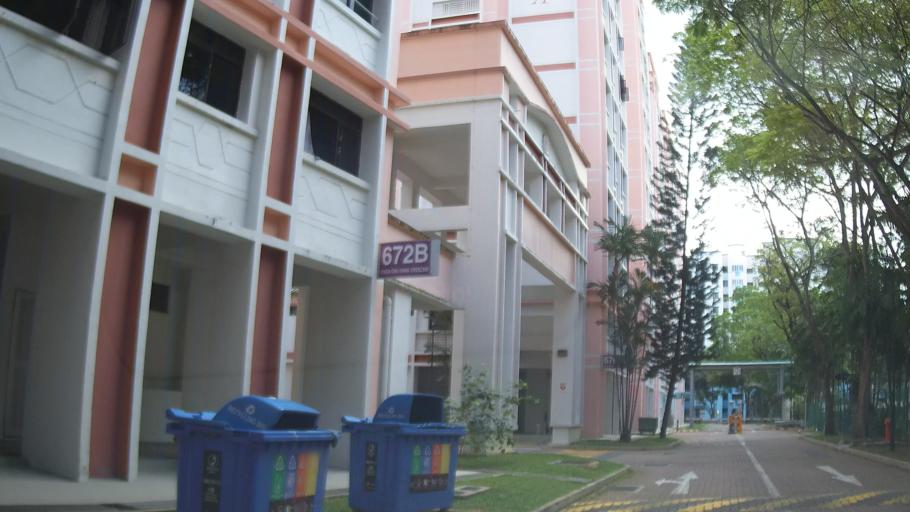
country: MY
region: Johor
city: Johor Bahru
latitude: 1.4022
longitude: 103.7471
